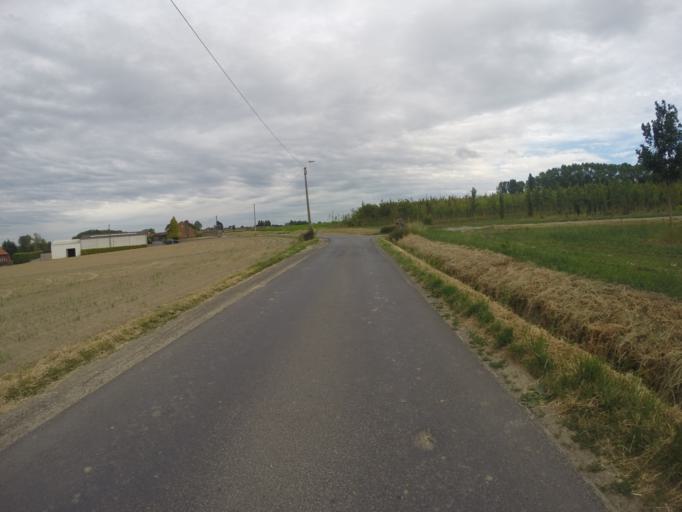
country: BE
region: Flanders
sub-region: Provincie West-Vlaanderen
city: Dentergem
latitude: 51.0018
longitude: 3.4068
